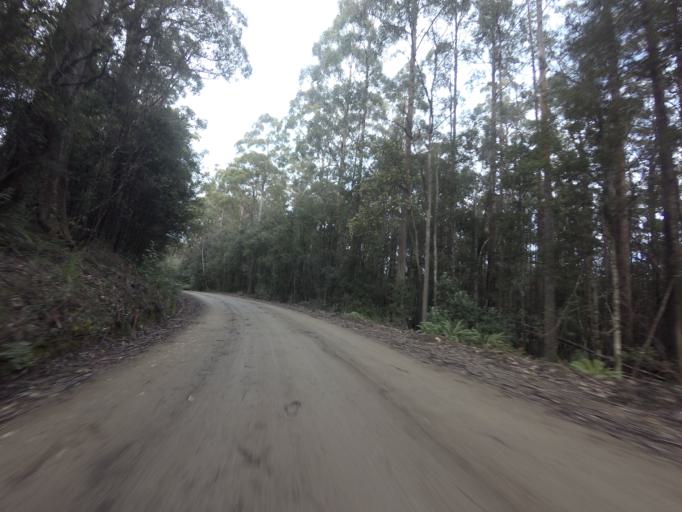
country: AU
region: Tasmania
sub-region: Huon Valley
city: Geeveston
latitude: -43.4950
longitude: 146.8801
